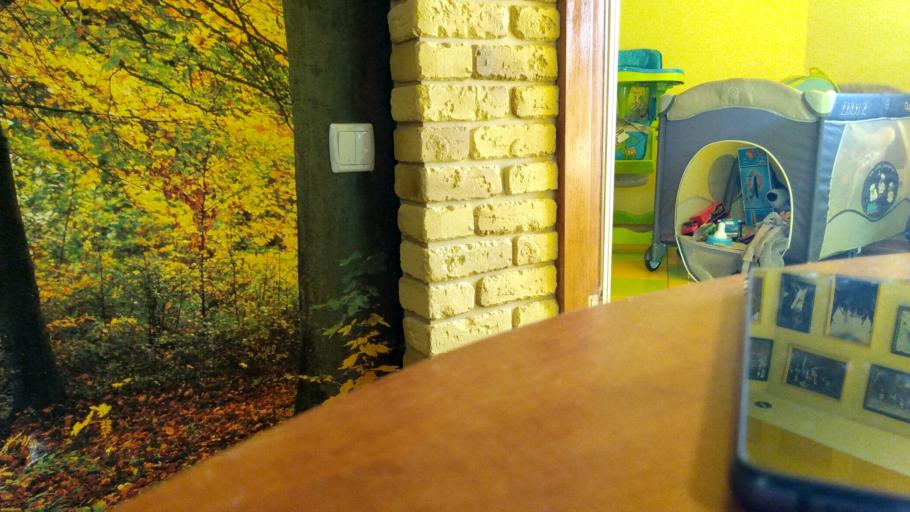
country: RU
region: Tverskaya
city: Likhoslavl'
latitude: 57.2567
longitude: 35.4163
